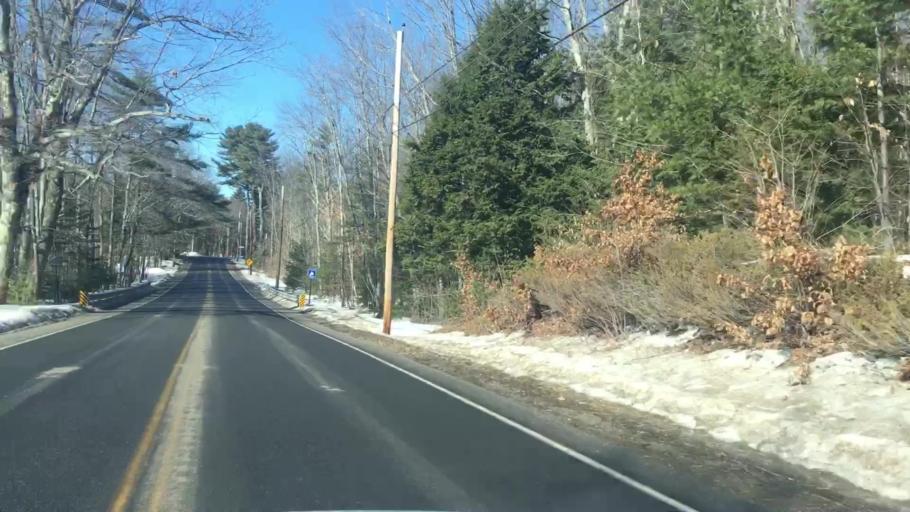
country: US
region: Maine
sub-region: Cumberland County
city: North Windham
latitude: 43.8144
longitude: -70.3811
